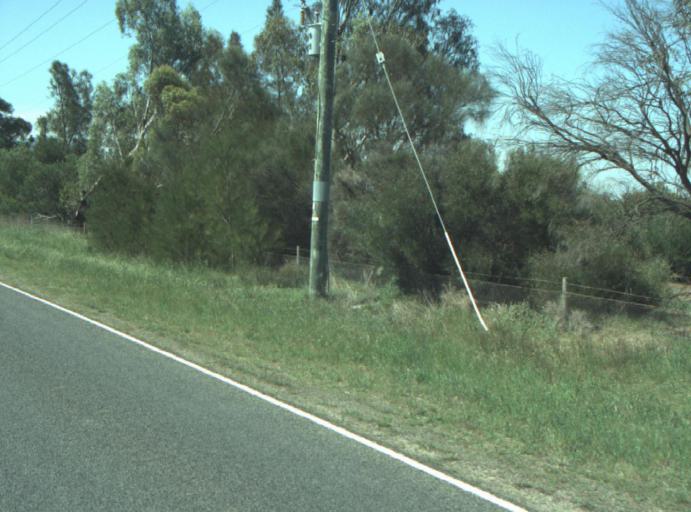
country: AU
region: Victoria
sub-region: Greater Geelong
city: Lara
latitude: -38.0019
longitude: 144.4001
